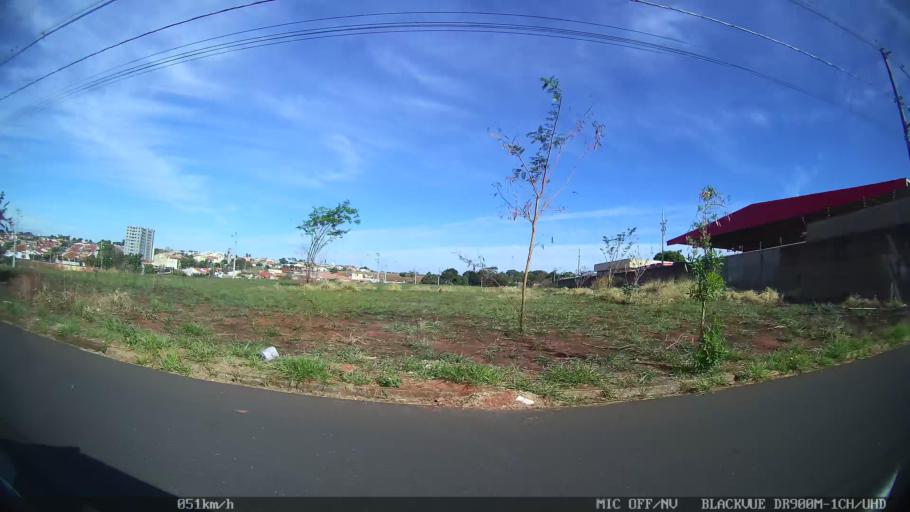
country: BR
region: Sao Paulo
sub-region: Sao Jose Do Rio Preto
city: Sao Jose do Rio Preto
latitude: -20.7898
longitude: -49.3526
